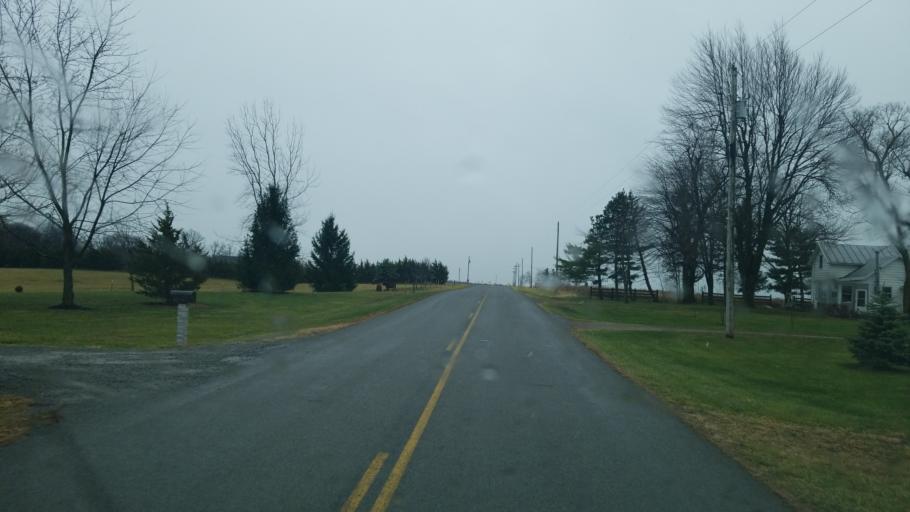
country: US
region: Ohio
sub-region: Logan County
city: Northwood
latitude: 40.4473
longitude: -83.6541
